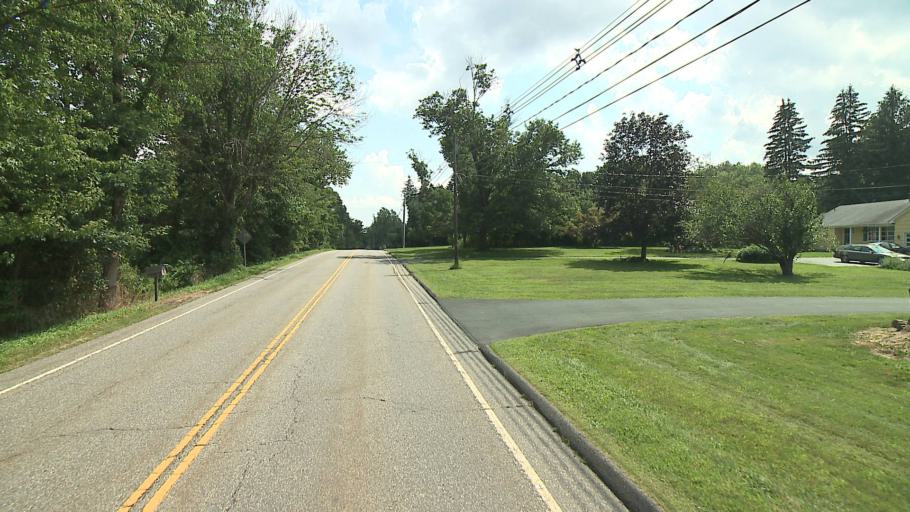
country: US
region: Connecticut
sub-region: Litchfield County
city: Bethlehem Village
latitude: 41.6807
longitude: -73.1659
